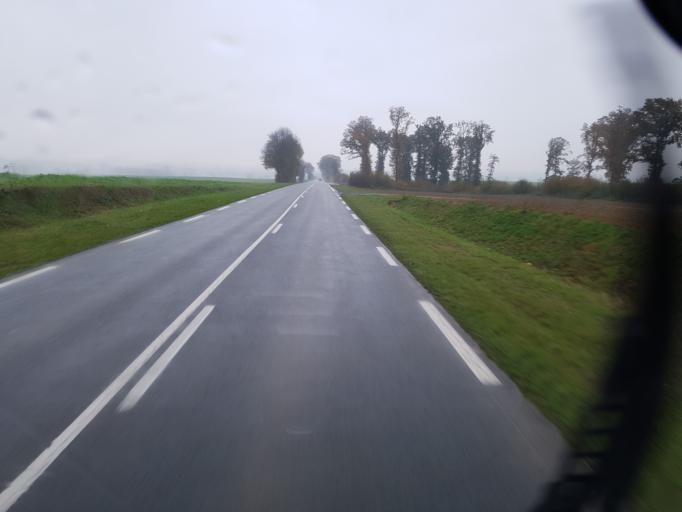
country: FR
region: Picardie
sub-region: Departement de l'Aisne
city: Omissy
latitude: 49.9052
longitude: 3.2601
